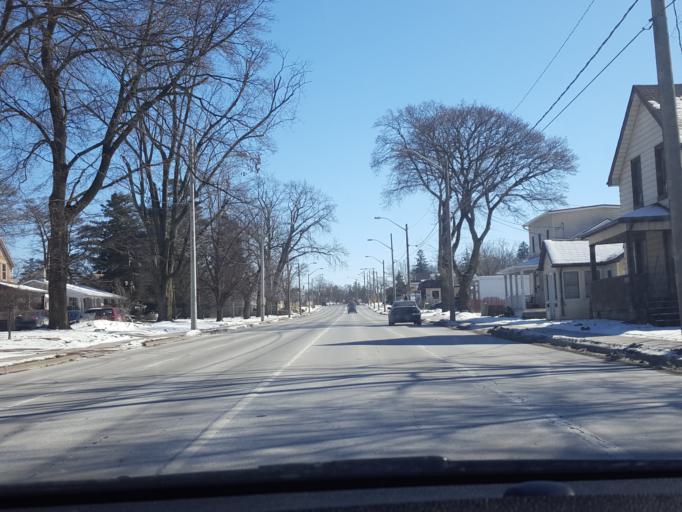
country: CA
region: Ontario
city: Cambridge
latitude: 43.3891
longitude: -80.3452
